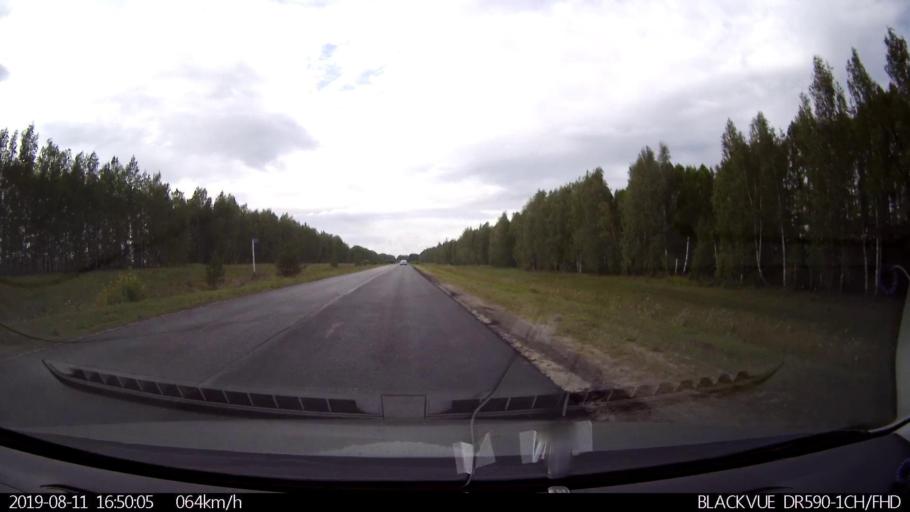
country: RU
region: Ulyanovsk
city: Mayna
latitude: 54.2258
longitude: 47.6913
